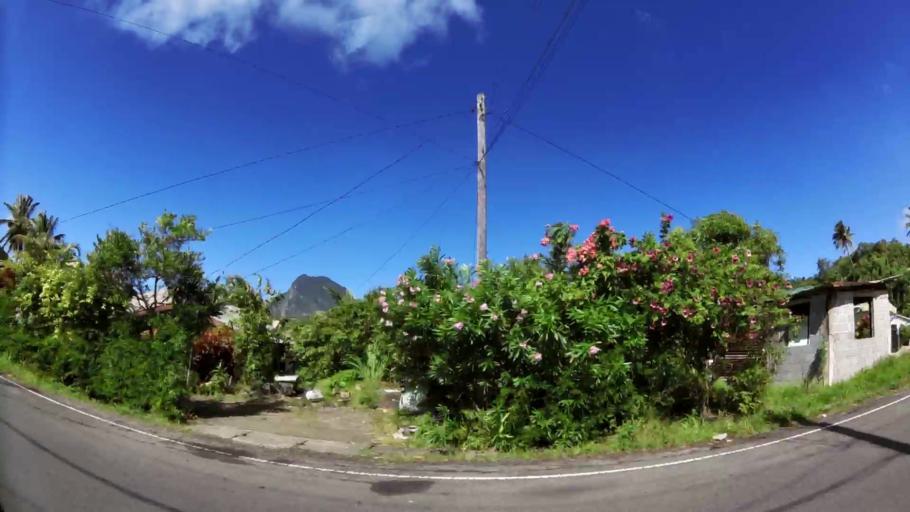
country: LC
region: Choiseul Quarter
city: Choiseul
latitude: 13.8013
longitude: -61.0372
